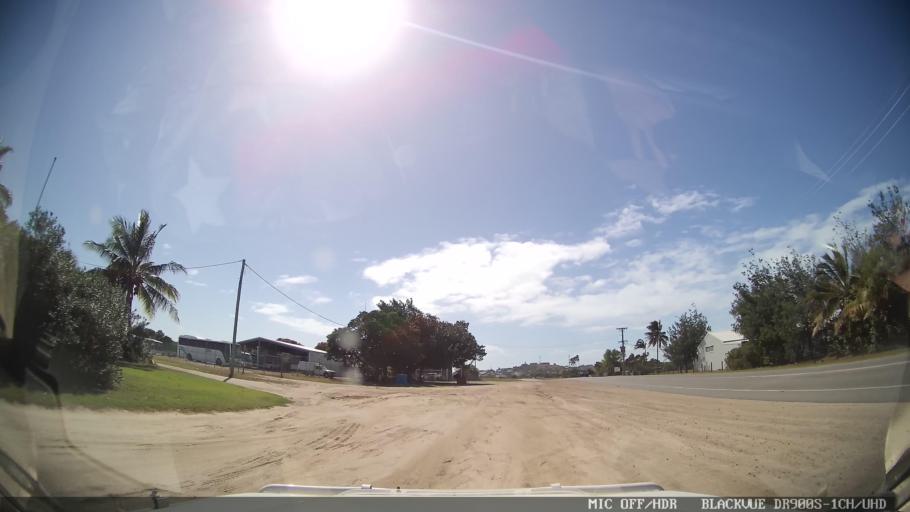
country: AU
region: Queensland
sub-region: Whitsunday
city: Bowen
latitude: -20.0132
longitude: 148.2240
